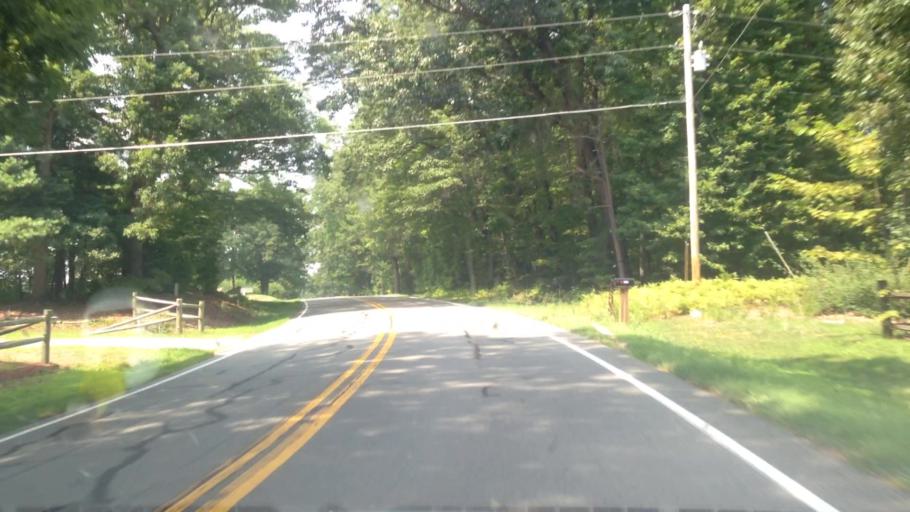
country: US
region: North Carolina
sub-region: Stokes County
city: Walnut Cove
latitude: 36.2699
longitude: -80.0883
